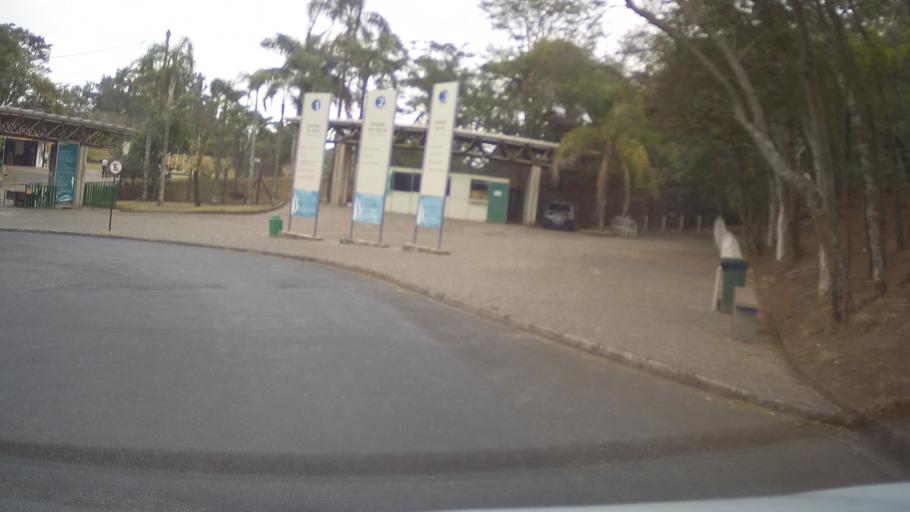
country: BR
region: Minas Gerais
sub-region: Belo Horizonte
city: Belo Horizonte
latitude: -19.9516
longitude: -43.9056
